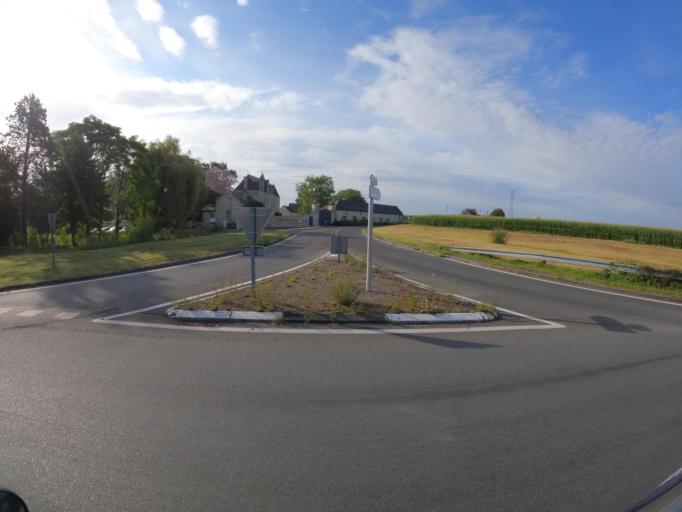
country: FR
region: Pays de la Loire
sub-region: Departement de Maine-et-Loire
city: Distre
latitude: 47.2255
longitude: -0.1405
